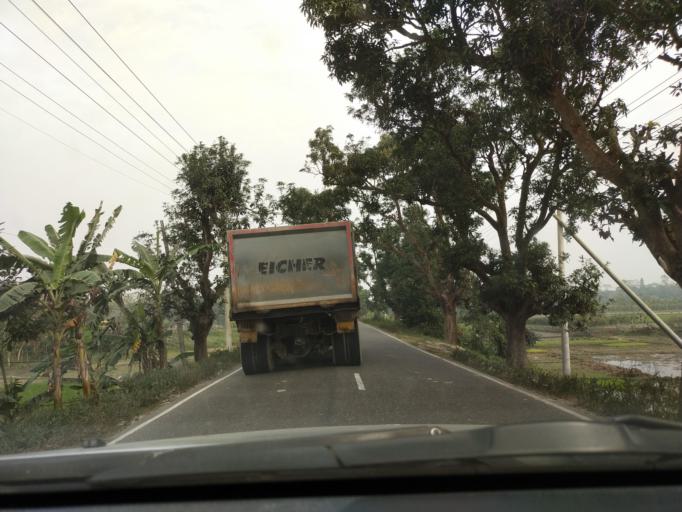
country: BD
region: Dhaka
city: Narsingdi
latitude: 24.0186
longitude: 90.7376
